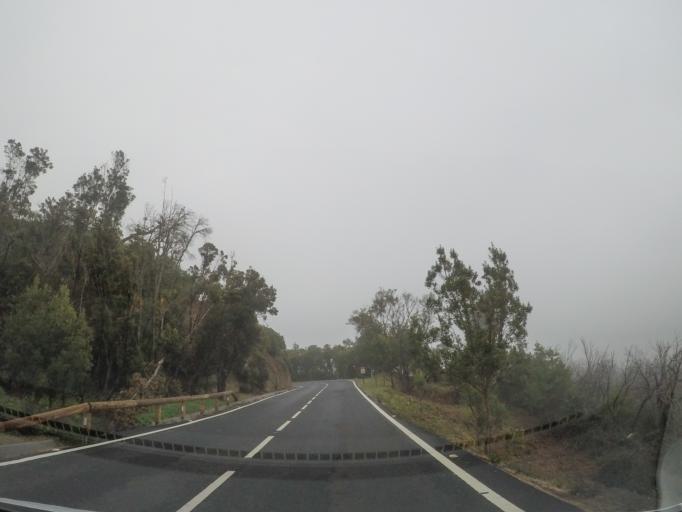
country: ES
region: Canary Islands
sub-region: Provincia de Santa Cruz de Tenerife
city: Alajero
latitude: 28.1209
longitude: -17.2503
